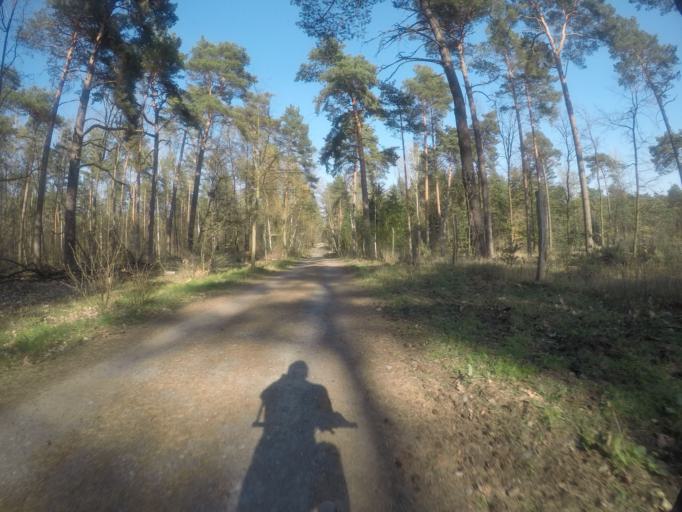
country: DE
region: Berlin
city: Wannsee
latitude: 52.4018
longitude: 13.1567
